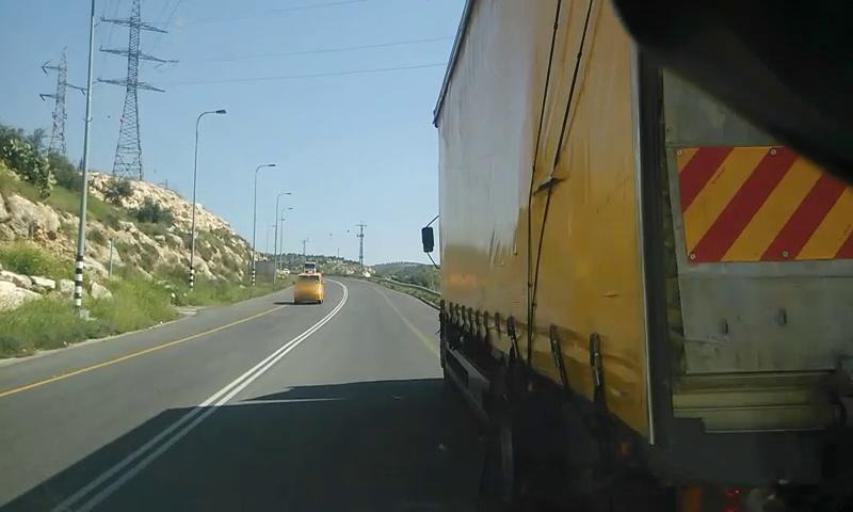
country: PS
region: West Bank
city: Idhna
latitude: 31.5687
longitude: 34.9878
